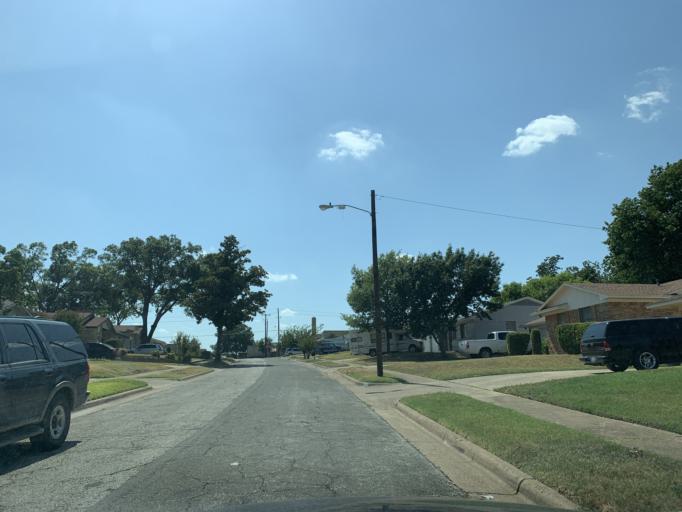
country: US
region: Texas
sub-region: Dallas County
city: Hutchins
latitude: 32.6749
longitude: -96.7955
